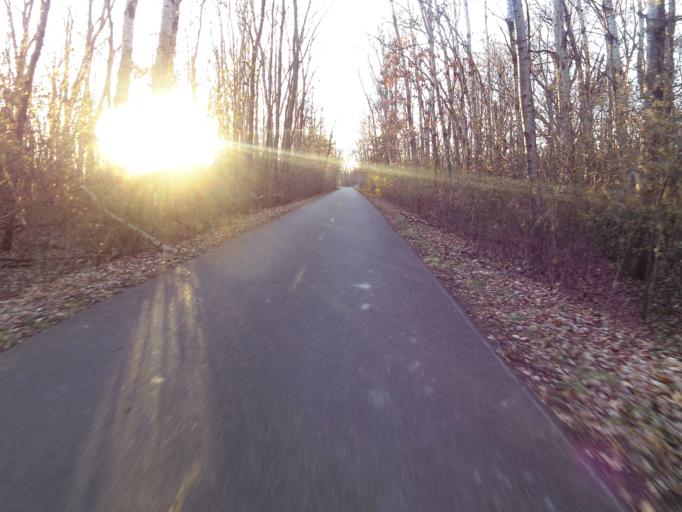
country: US
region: Minnesota
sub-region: Washington County
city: Grant
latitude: 45.1161
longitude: -92.8469
